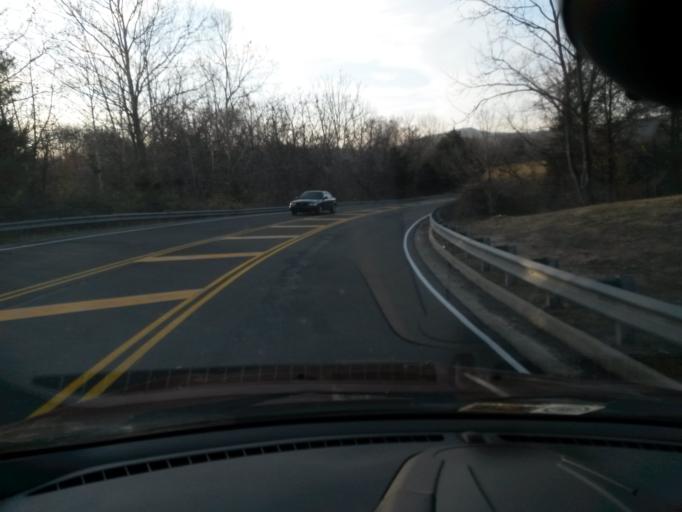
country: US
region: Virginia
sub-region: Roanoke County
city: Hollins
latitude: 37.3370
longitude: -79.9659
